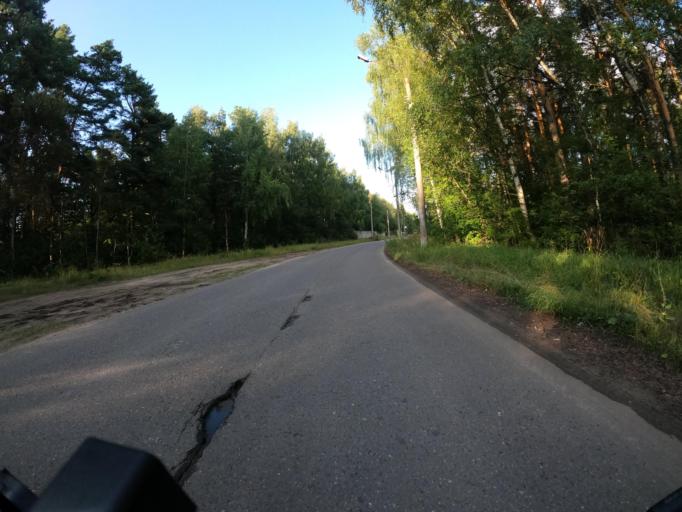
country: RU
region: Moskovskaya
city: Beloozerskiy
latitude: 55.4568
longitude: 38.4923
